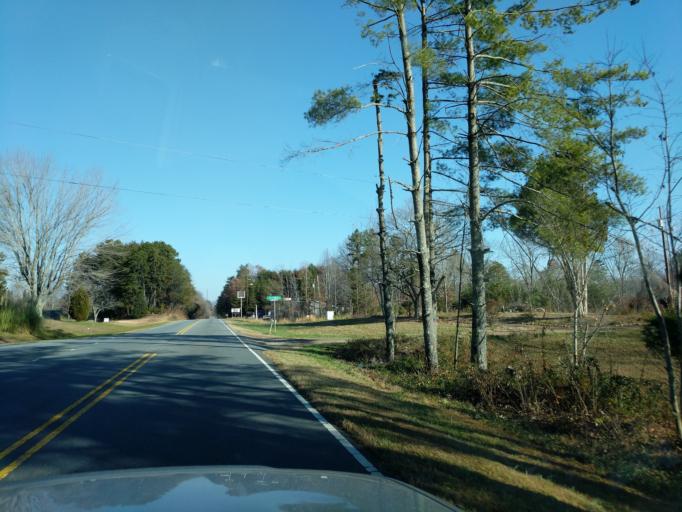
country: US
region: North Carolina
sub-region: Rutherford County
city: Rutherfordton
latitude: 35.4773
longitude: -81.9813
